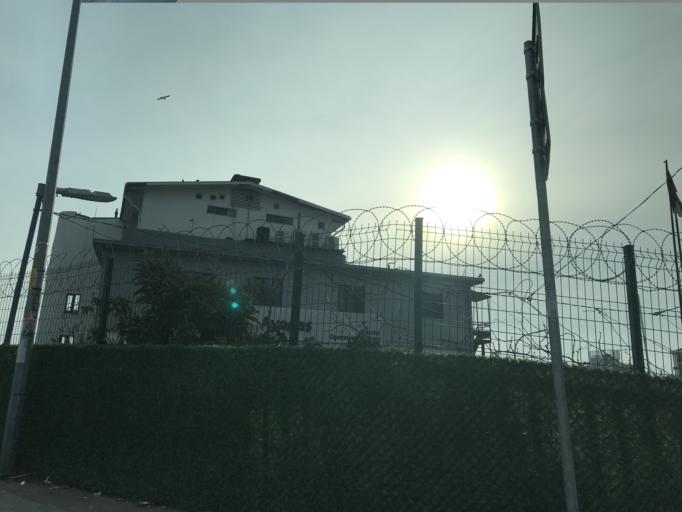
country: TR
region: Istanbul
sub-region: Atasehir
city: Atasehir
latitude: 40.9662
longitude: 29.1060
